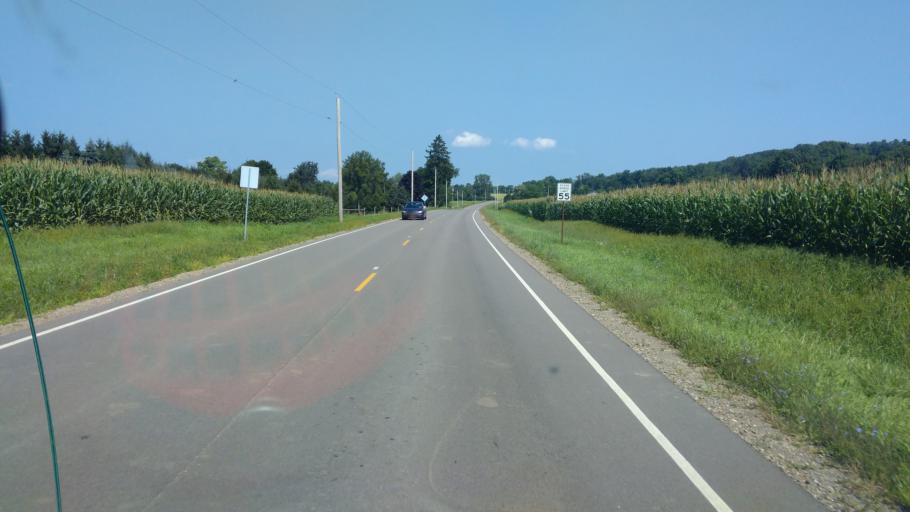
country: US
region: New York
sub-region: Allegany County
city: Belmont
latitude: 42.2438
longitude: -78.0408
